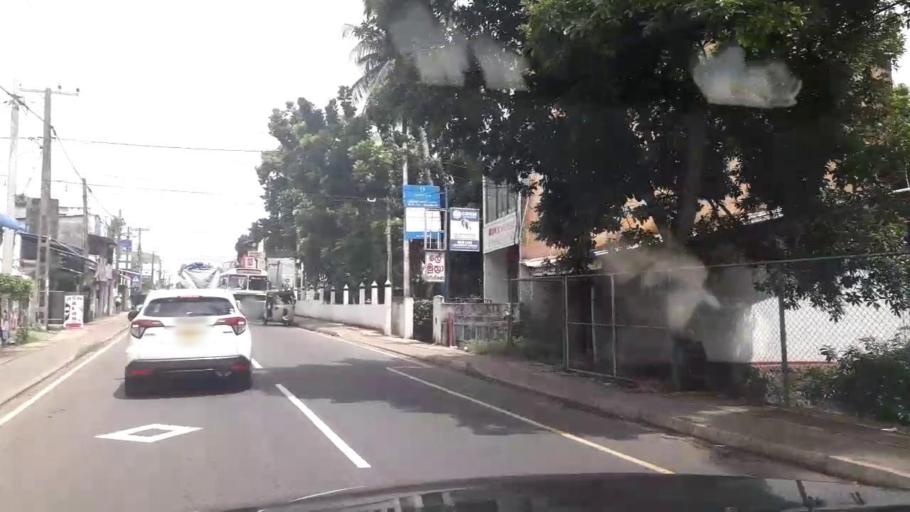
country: LK
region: Western
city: Moratuwa
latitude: 6.7533
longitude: 79.8996
